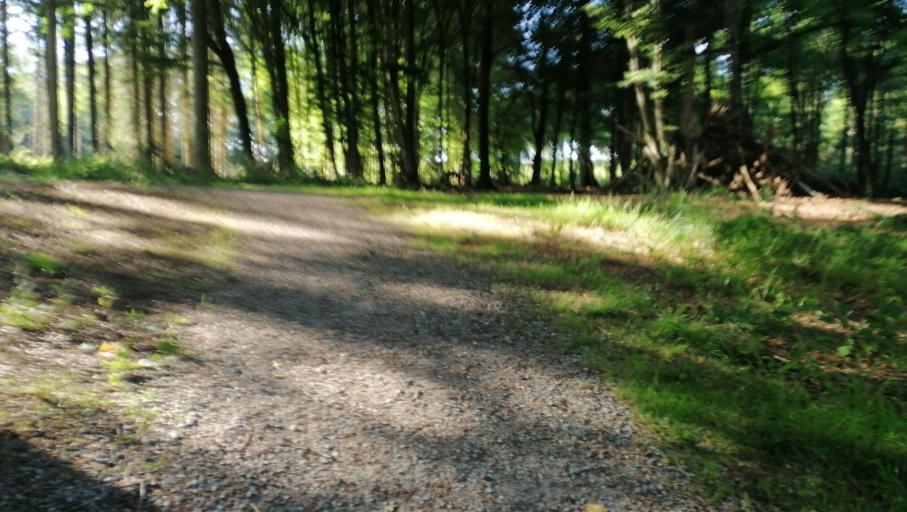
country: FR
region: Nord-Pas-de-Calais
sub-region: Departement du Nord
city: Landrecies
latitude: 50.1682
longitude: 3.7054
